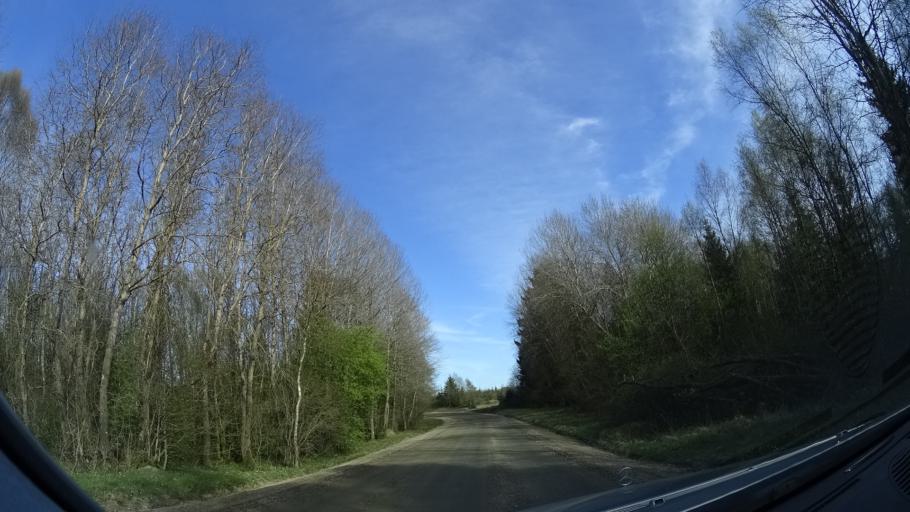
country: SE
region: Skane
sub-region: Hassleholms Kommun
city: Sosdala
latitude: 56.0869
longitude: 13.6761
